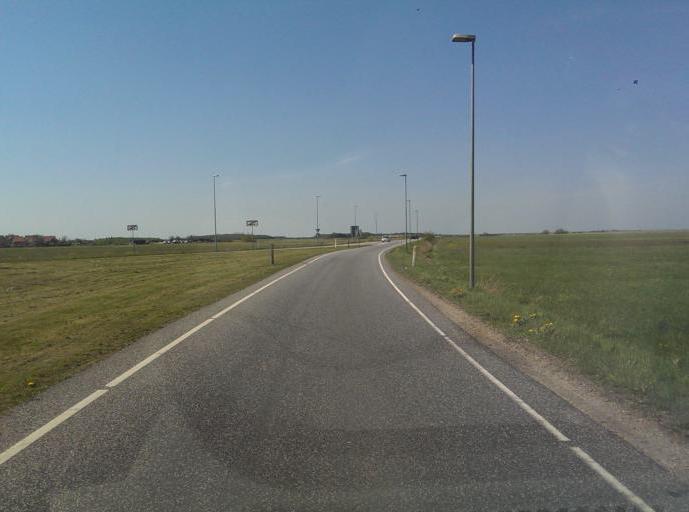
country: DK
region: South Denmark
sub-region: Esbjerg Kommune
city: Ribe
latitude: 55.3354
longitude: 8.7676
